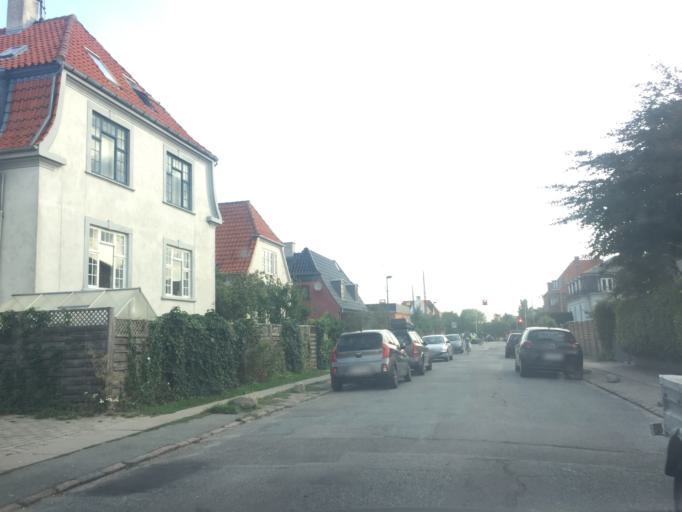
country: DK
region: Capital Region
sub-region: Kobenhavn
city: Vanlose
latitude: 55.7071
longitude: 12.4843
